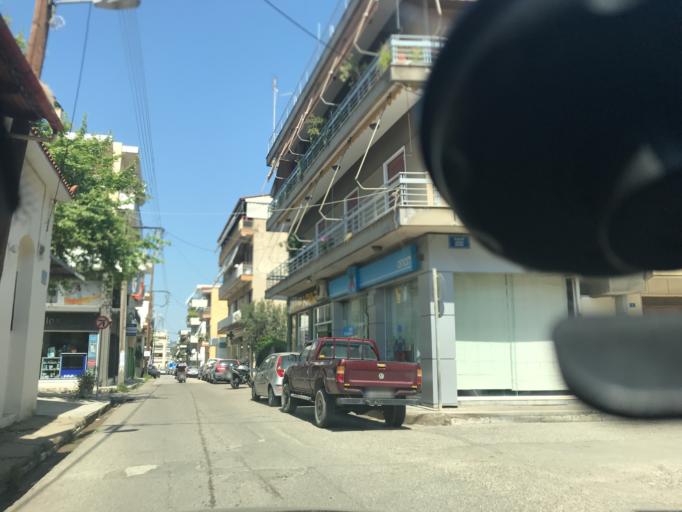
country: GR
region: West Greece
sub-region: Nomos Ileias
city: Pyrgos
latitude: 37.6730
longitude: 21.4437
